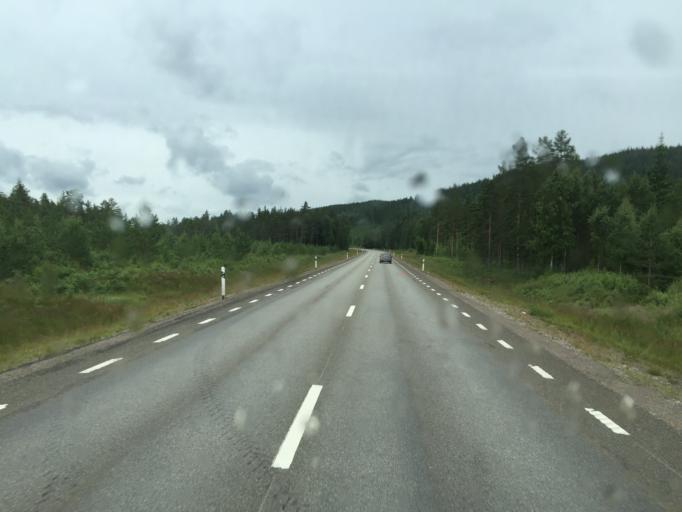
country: SE
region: Dalarna
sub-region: Malung-Saelens kommun
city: Malung
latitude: 60.6414
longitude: 13.6221
